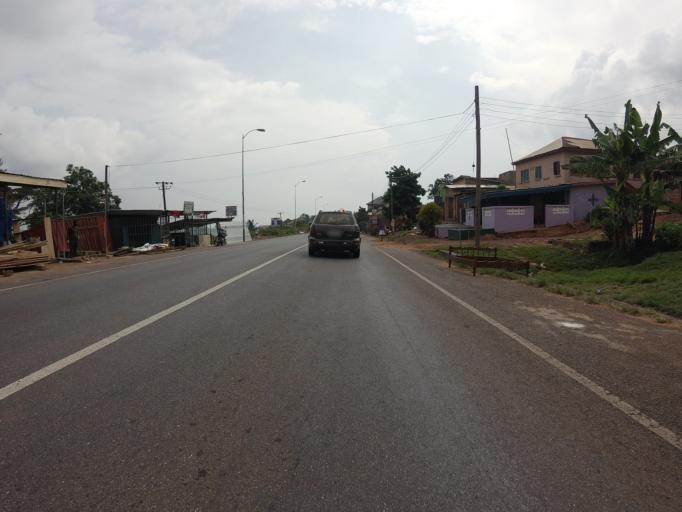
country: GH
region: Eastern
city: Aburi
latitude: 5.8486
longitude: -0.1725
